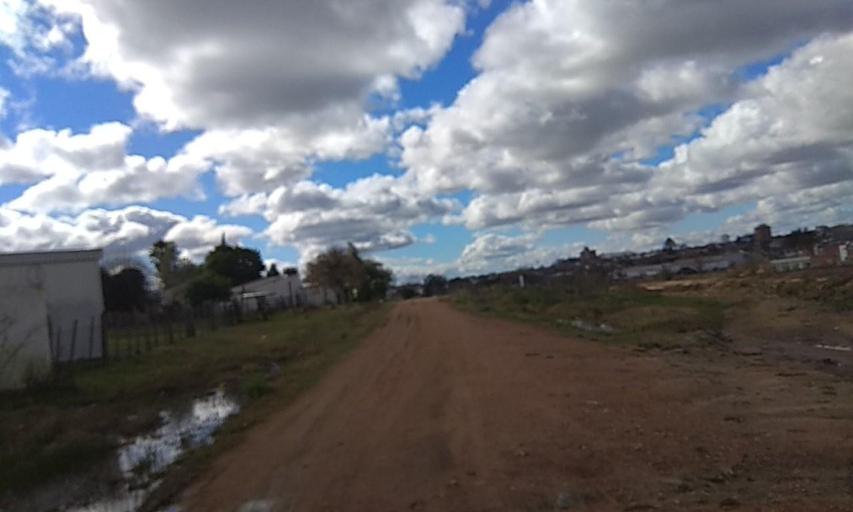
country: UY
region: Florida
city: Florida
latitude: -34.0956
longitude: -56.2300
